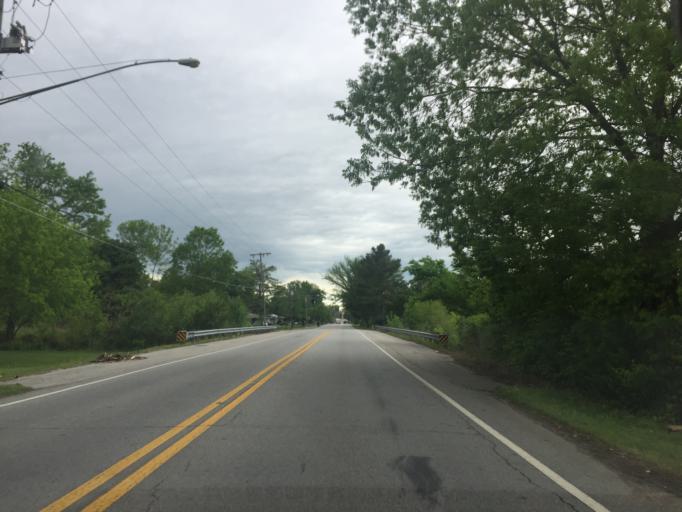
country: US
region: Tennessee
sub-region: Hamilton County
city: East Brainerd
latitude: 35.0528
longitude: -85.1628
